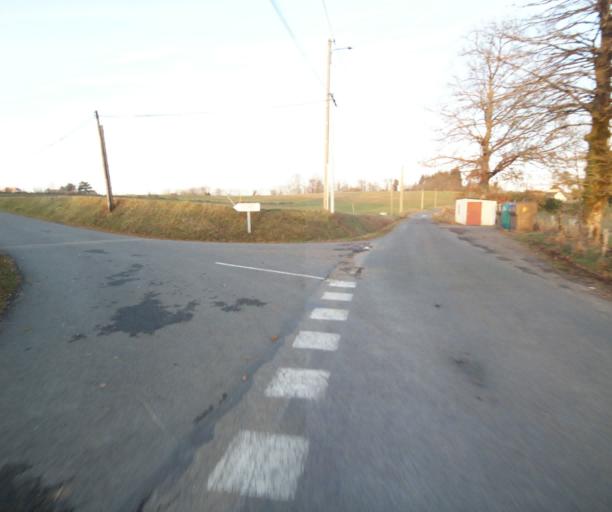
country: FR
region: Limousin
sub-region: Departement de la Correze
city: Laguenne
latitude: 45.2249
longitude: 1.8270
